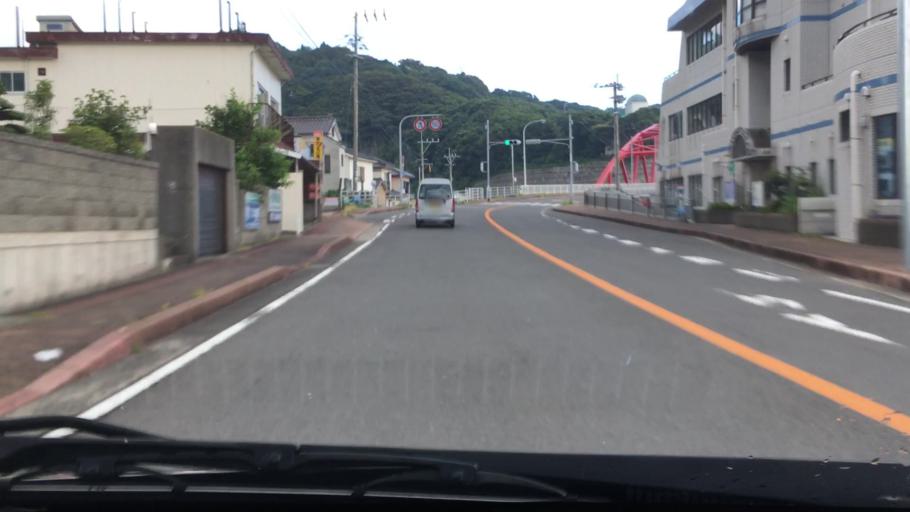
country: JP
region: Nagasaki
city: Togitsu
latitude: 32.8807
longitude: 129.6798
